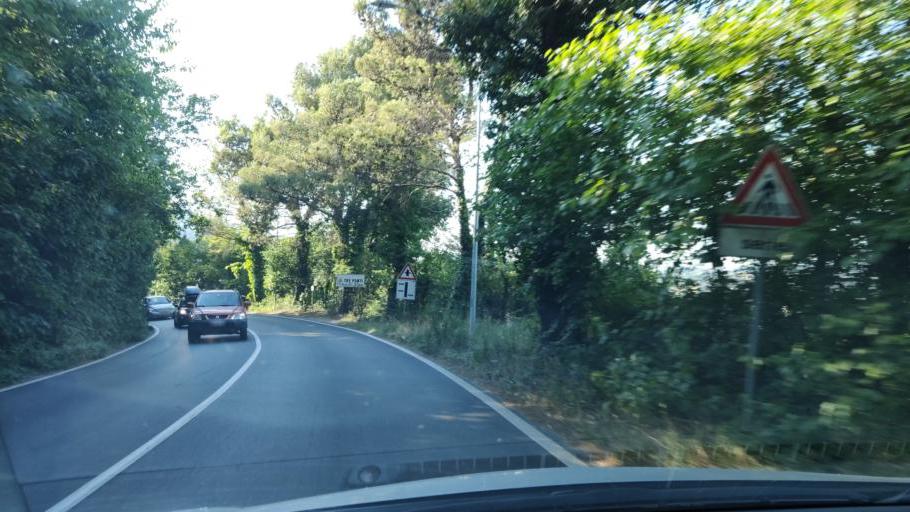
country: IT
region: Umbria
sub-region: Provincia di Terni
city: Narni
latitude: 42.5202
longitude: 12.5210
